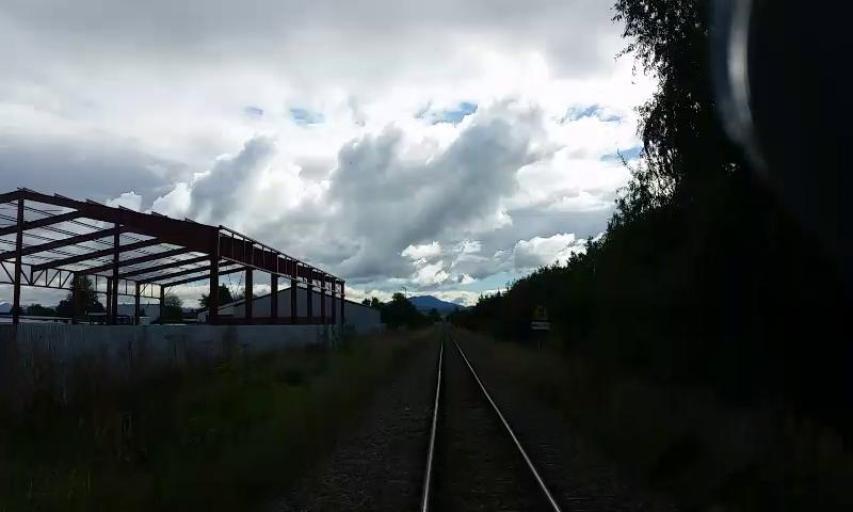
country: NZ
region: Canterbury
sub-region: Waimakariri District
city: Woodend
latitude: -43.3140
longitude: 172.6009
